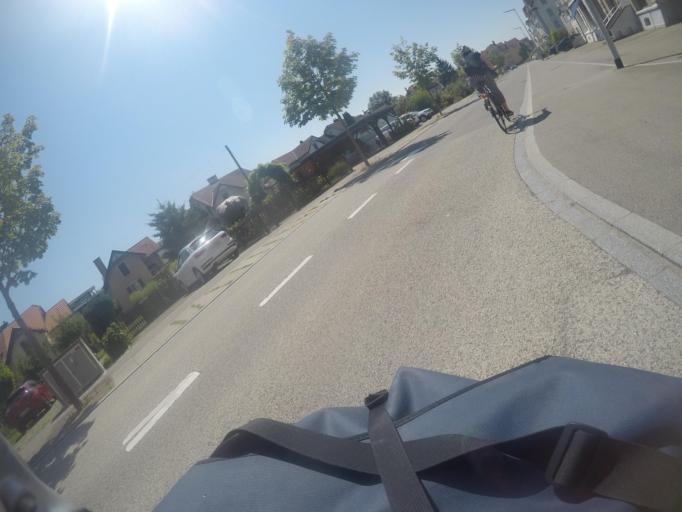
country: CH
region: Thurgau
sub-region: Arbon District
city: Arbon
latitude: 47.5096
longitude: 9.4283
